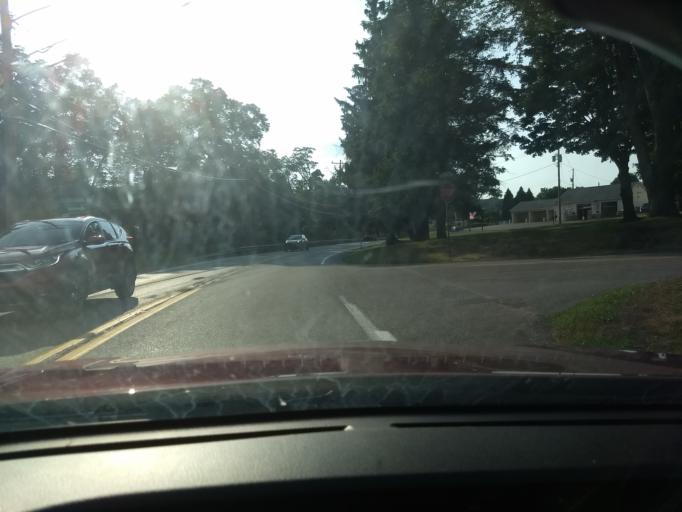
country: US
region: Pennsylvania
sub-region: Allegheny County
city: Bakerstown
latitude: 40.6326
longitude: -79.9371
